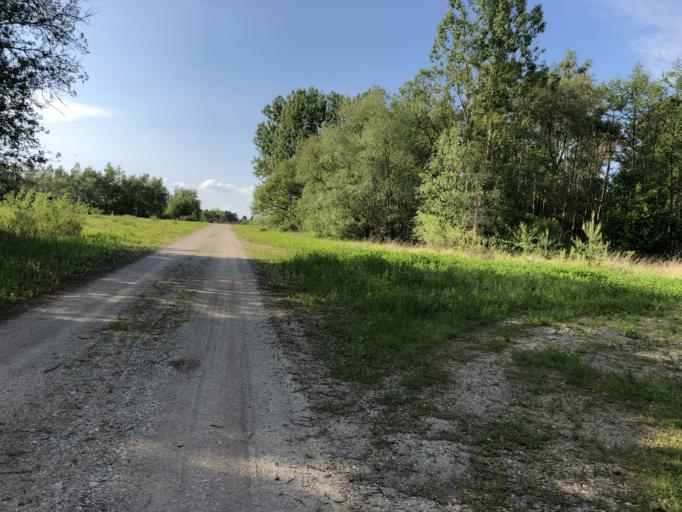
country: DE
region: Bavaria
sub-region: Upper Franconia
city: Memmelsdorf
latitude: 49.9118
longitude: 10.9465
